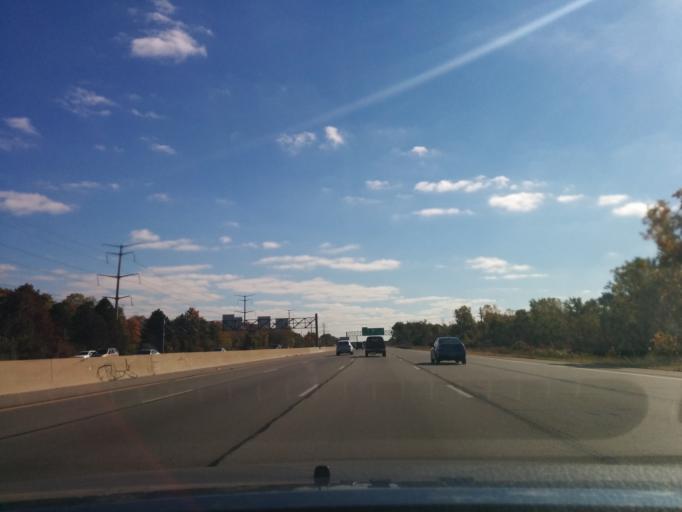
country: US
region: Michigan
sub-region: Oakland County
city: Novi
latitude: 42.4863
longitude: -83.4687
